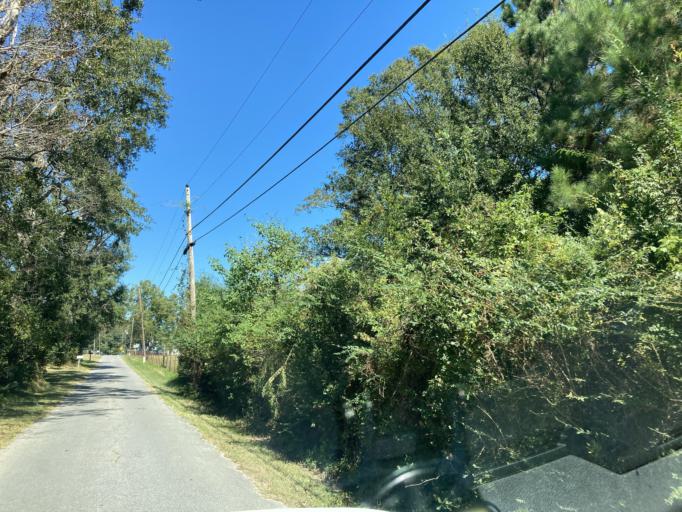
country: US
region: Mississippi
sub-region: Jackson County
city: Saint Martin
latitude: 30.4697
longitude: -88.8750
